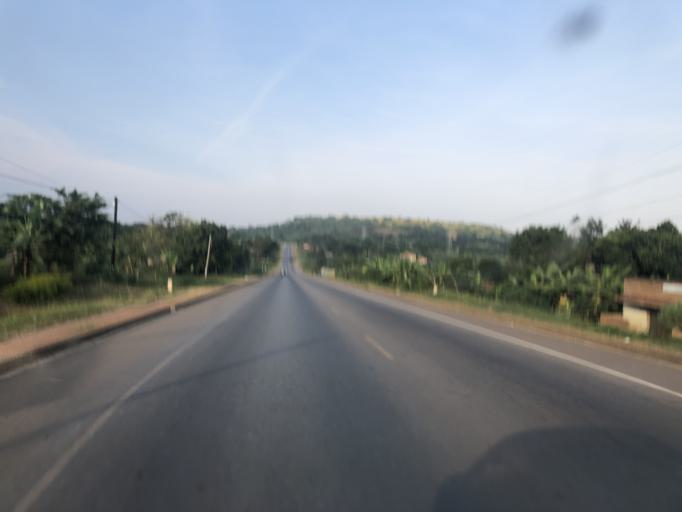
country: UG
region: Central Region
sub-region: Mpigi District
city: Mpigi
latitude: 0.1723
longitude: 32.2655
